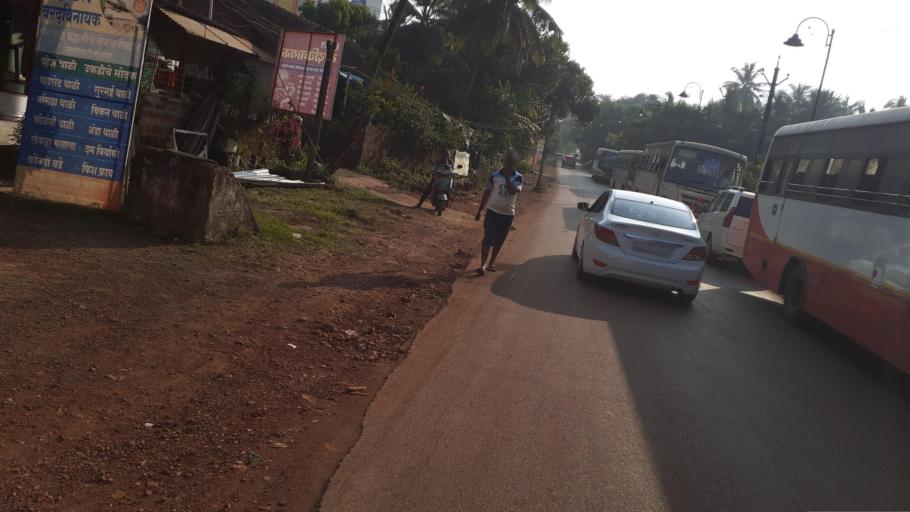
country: IN
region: Maharashtra
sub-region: Ratnagiri
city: Ratnagiri
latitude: 17.1471
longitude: 73.2716
